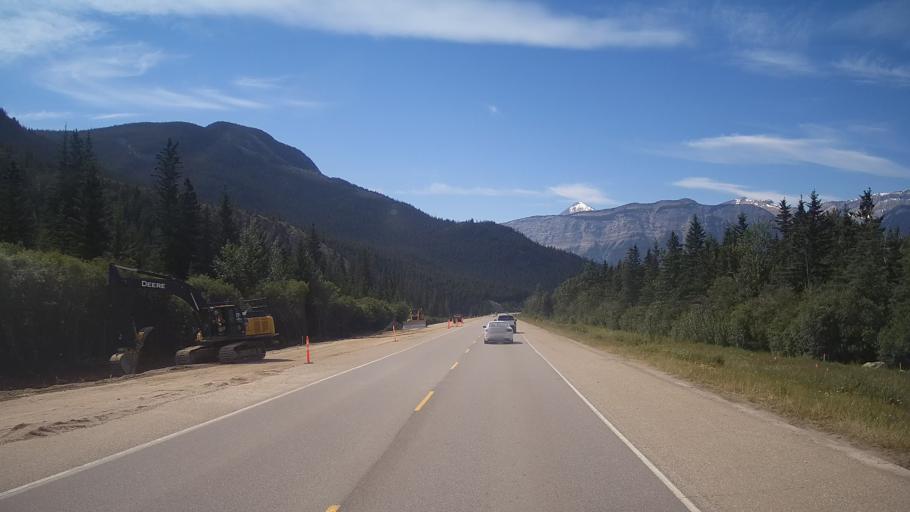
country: CA
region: Alberta
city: Jasper Park Lodge
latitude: 53.0600
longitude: -118.0671
